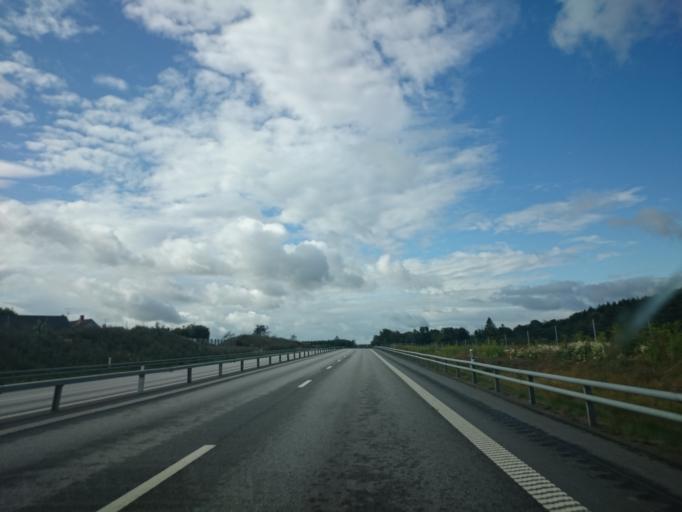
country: SE
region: Skane
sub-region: Horby Kommun
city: Hoerby
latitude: 55.8883
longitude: 13.7181
